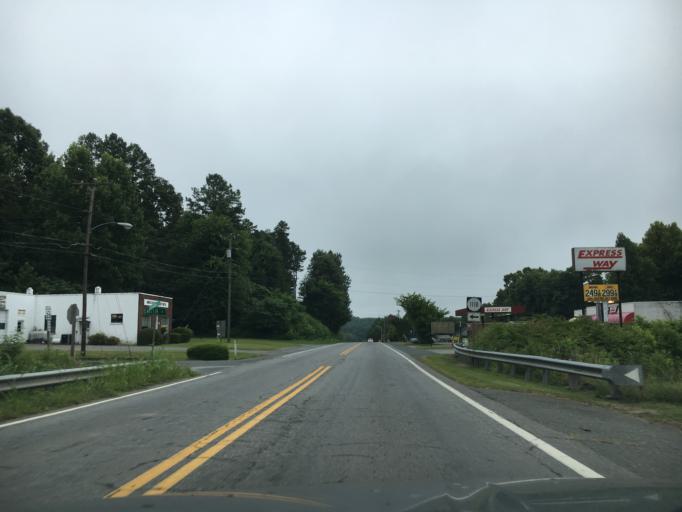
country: US
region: Virginia
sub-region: Campbell County
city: Brookneal
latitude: 37.0459
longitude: -78.9451
